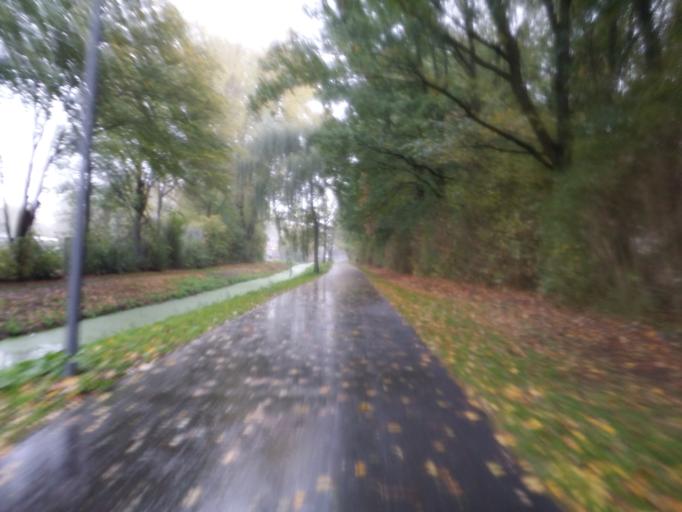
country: DE
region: Bremen
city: Bremen
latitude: 53.0363
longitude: 8.8155
